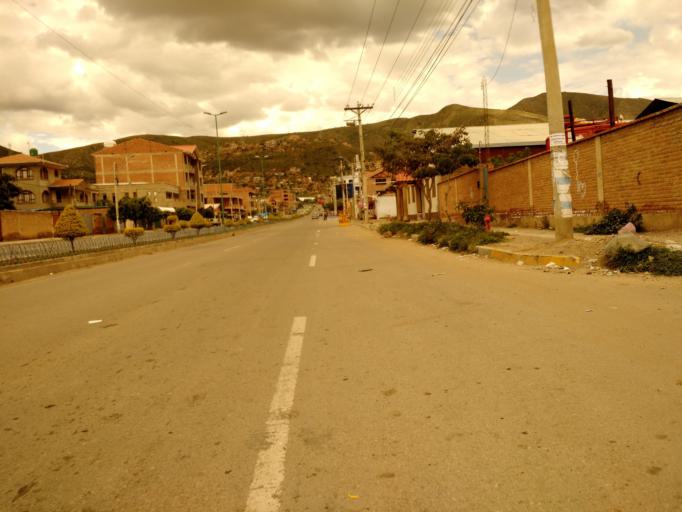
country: BO
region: Cochabamba
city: Cochabamba
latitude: -17.4233
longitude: -66.1269
